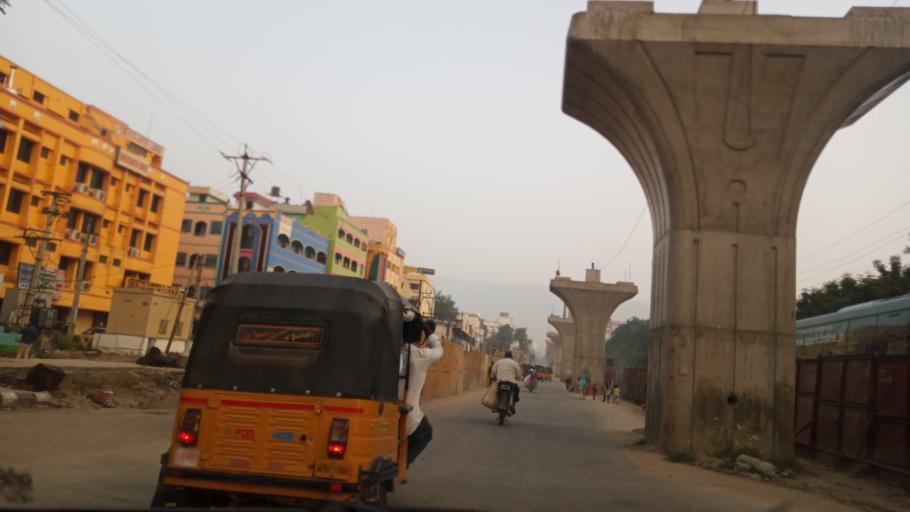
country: IN
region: Andhra Pradesh
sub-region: Chittoor
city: Tirupati
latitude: 13.6314
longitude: 79.4280
